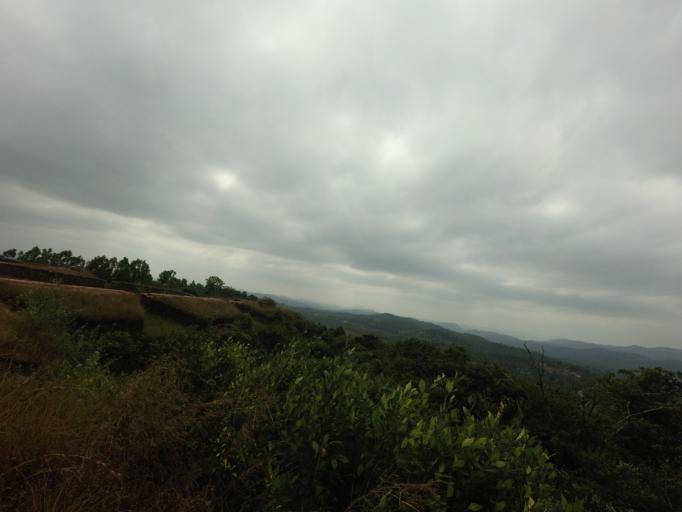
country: IN
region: Karnataka
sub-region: Hassan
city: Sakleshpur
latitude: 12.9174
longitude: 75.7579
